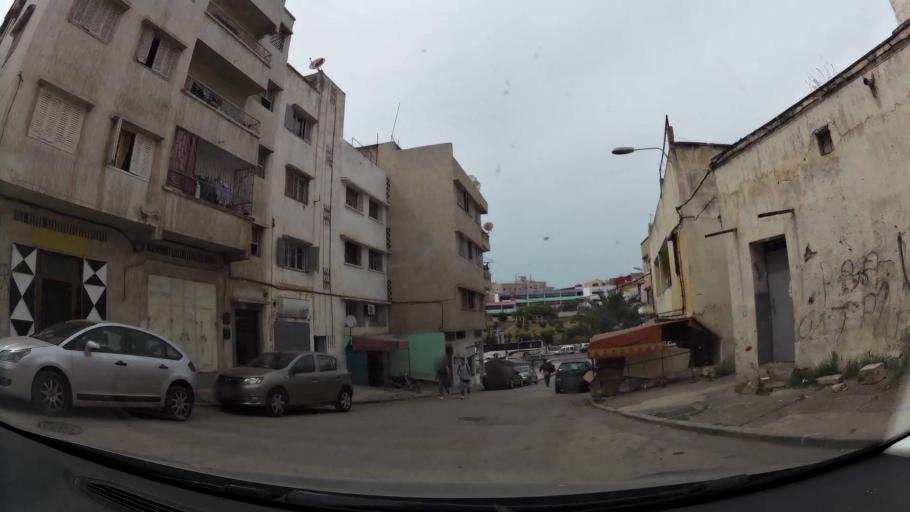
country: MA
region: Rabat-Sale-Zemmour-Zaer
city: Sale
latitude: 34.0342
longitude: -6.8051
